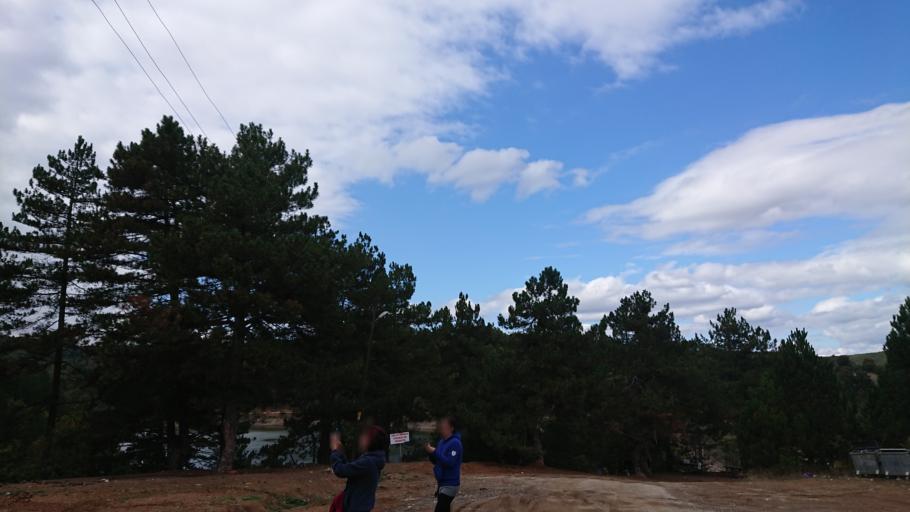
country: TR
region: Bilecik
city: Pazaryeri
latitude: 40.0149
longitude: 29.7968
